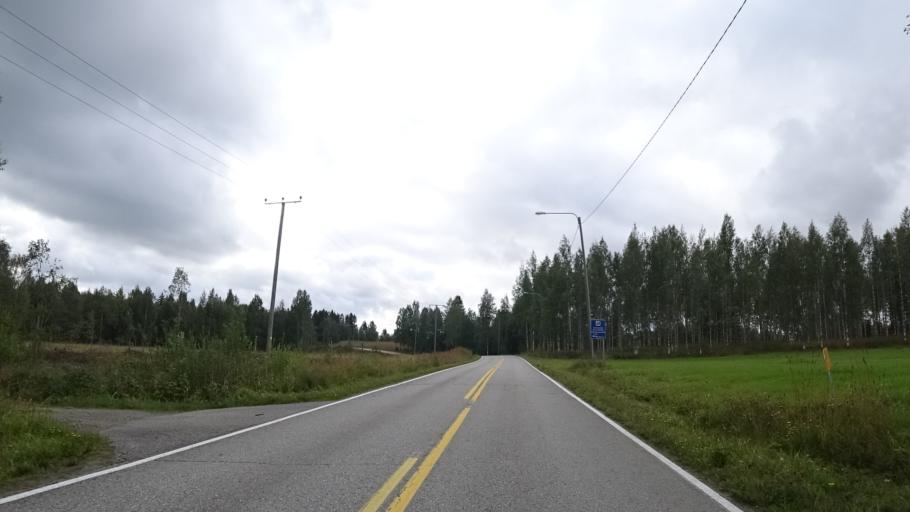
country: FI
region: North Karelia
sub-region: Joensuu
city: Ilomantsi
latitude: 62.9370
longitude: 31.2836
